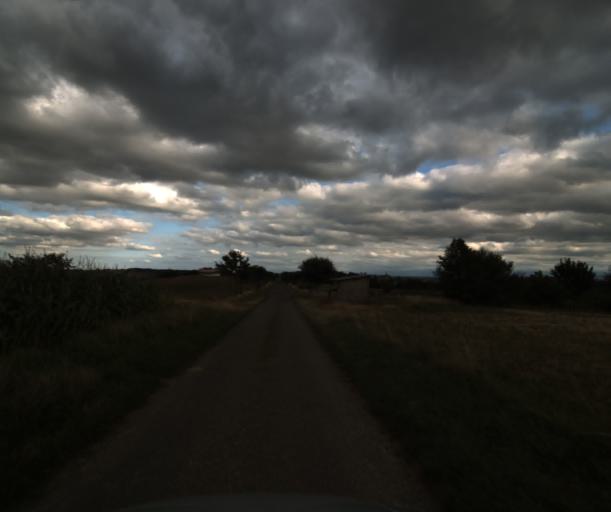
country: FR
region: Midi-Pyrenees
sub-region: Departement de la Haute-Garonne
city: Le Fauga
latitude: 43.3944
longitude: 1.3184
